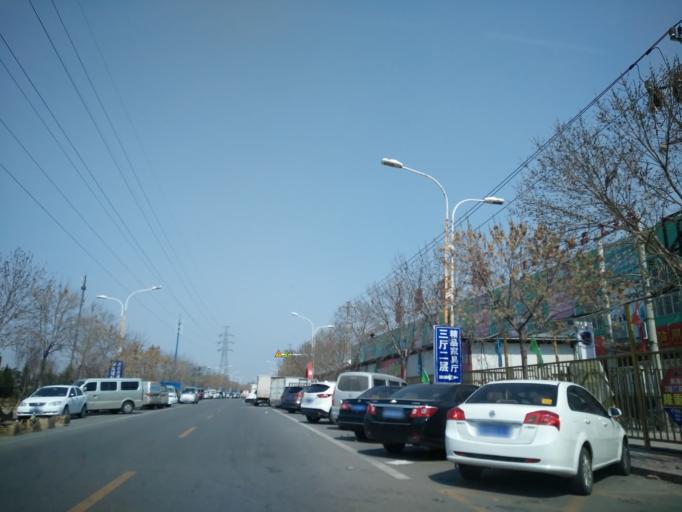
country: CN
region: Beijing
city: Qingyundian
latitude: 39.7564
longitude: 116.5342
